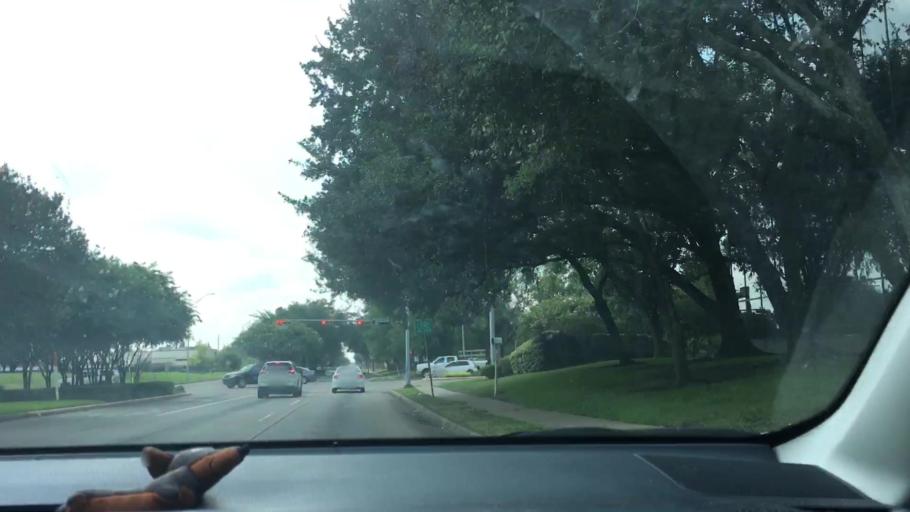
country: US
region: Texas
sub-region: Harris County
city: Bunker Hill Village
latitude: 29.7284
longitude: -95.5718
